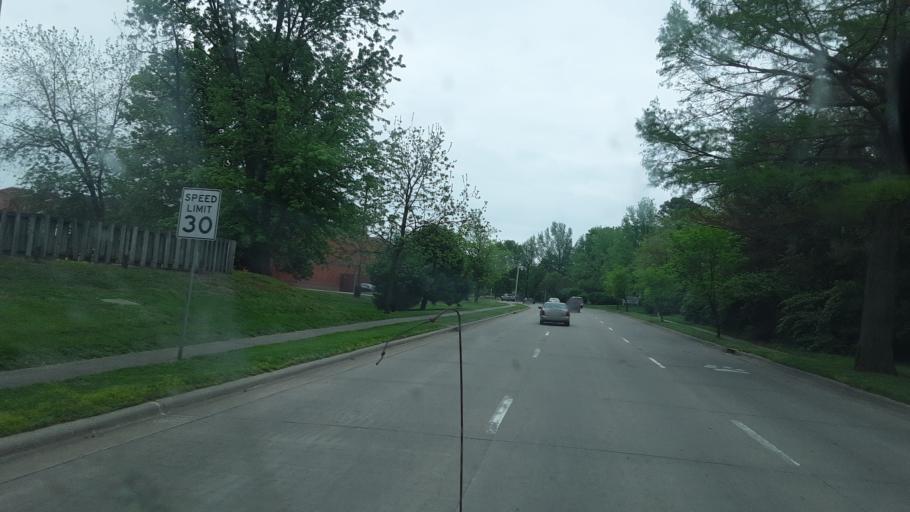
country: US
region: Illinois
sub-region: Jackson County
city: Carbondale
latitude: 37.7257
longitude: -89.2305
